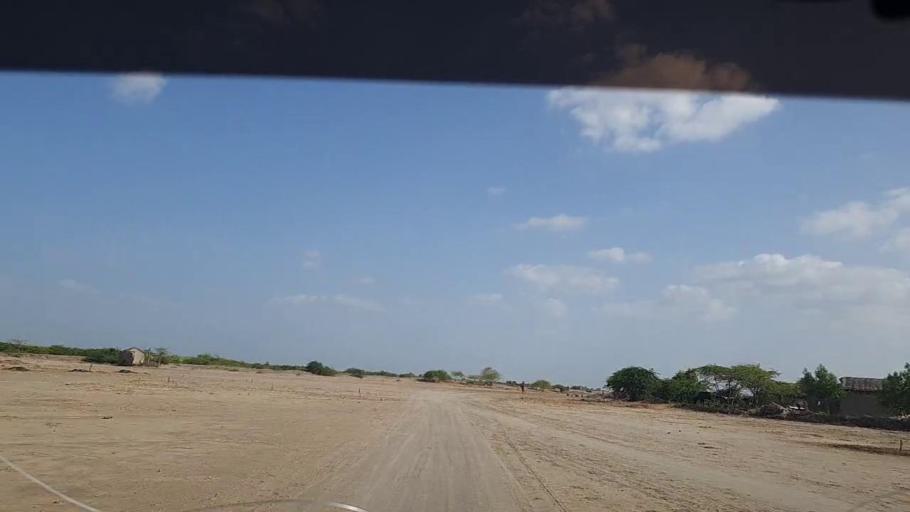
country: PK
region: Sindh
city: Kadhan
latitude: 24.4582
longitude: 68.8573
